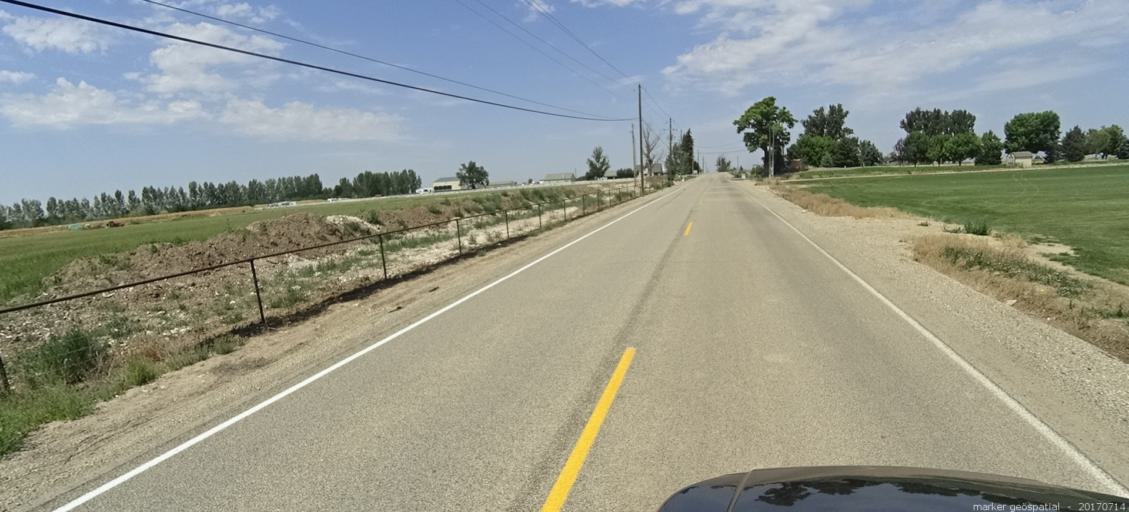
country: US
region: Idaho
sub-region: Ada County
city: Kuna
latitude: 43.5379
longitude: -116.3543
